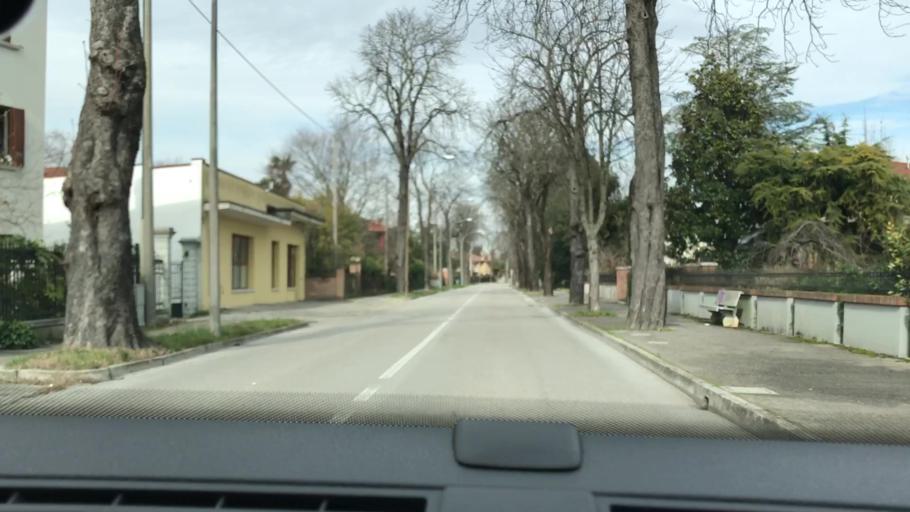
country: IT
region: Veneto
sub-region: Provincia di Venezia
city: Santo Stino di Livenza
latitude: 45.7240
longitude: 12.6806
